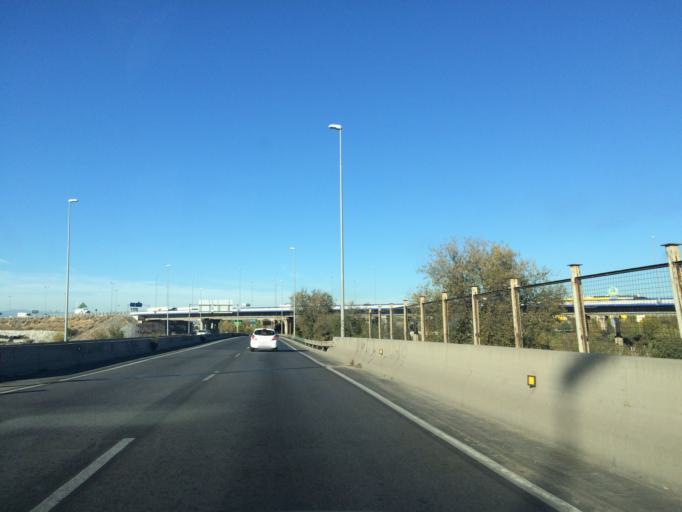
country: ES
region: Madrid
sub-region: Provincia de Madrid
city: Mostoles
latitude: 40.3360
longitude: -3.8516
